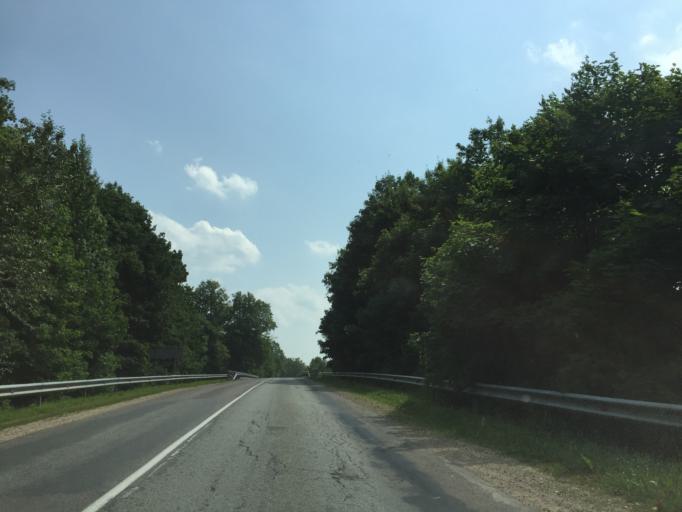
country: LV
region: Jelgava
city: Jelgava
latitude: 56.6893
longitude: 23.7194
